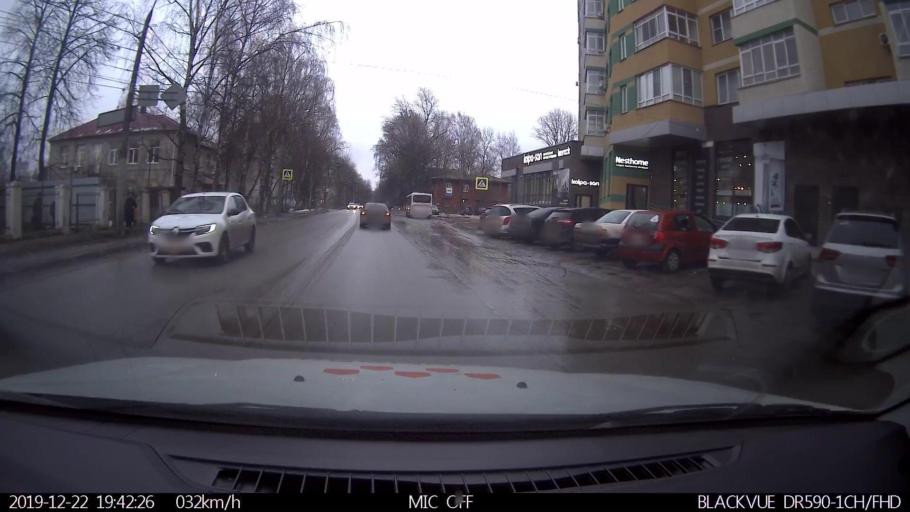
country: RU
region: Nizjnij Novgorod
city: Nizhniy Novgorod
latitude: 56.3133
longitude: 44.0321
